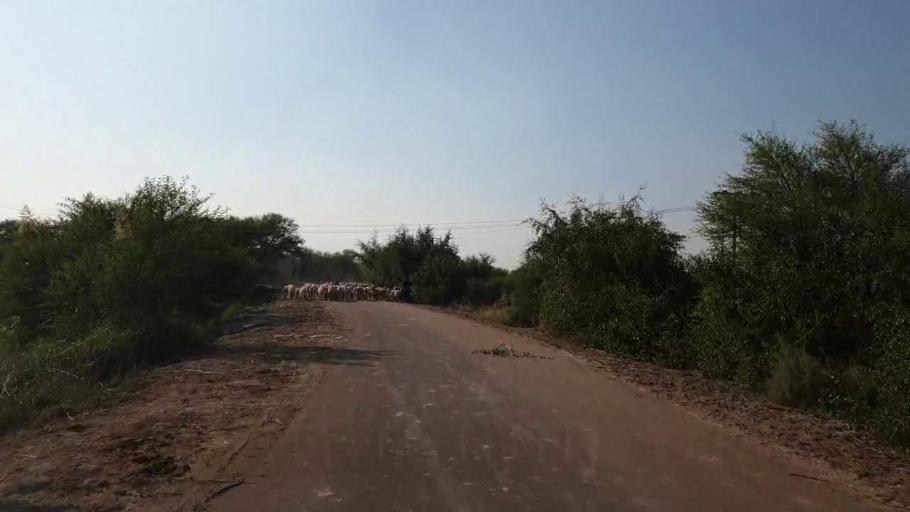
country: PK
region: Sindh
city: Sehwan
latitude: 26.4374
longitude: 67.7897
